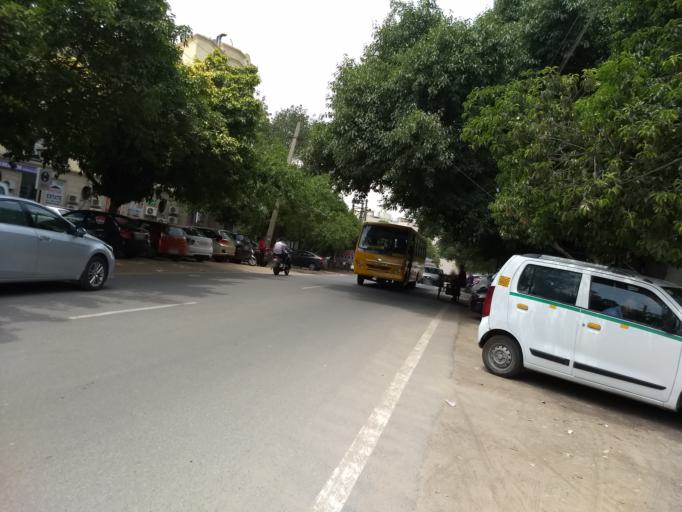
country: IN
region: Haryana
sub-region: Gurgaon
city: Gurgaon
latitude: 28.4947
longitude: 77.1038
